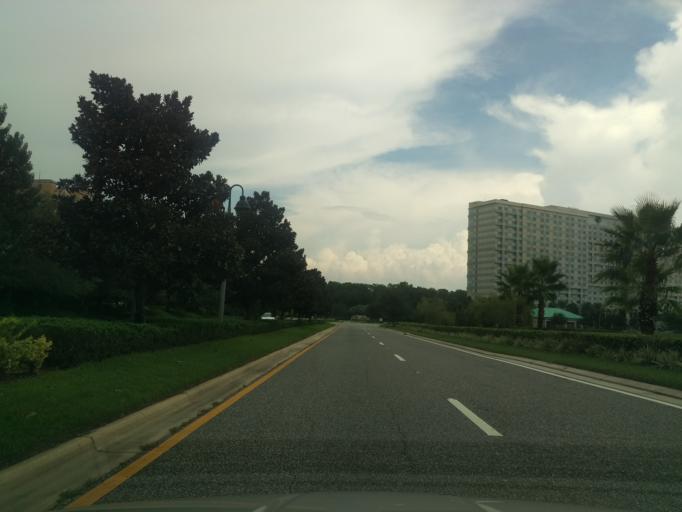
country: US
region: Florida
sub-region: Osceola County
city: Celebration
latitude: 28.3571
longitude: -81.5375
